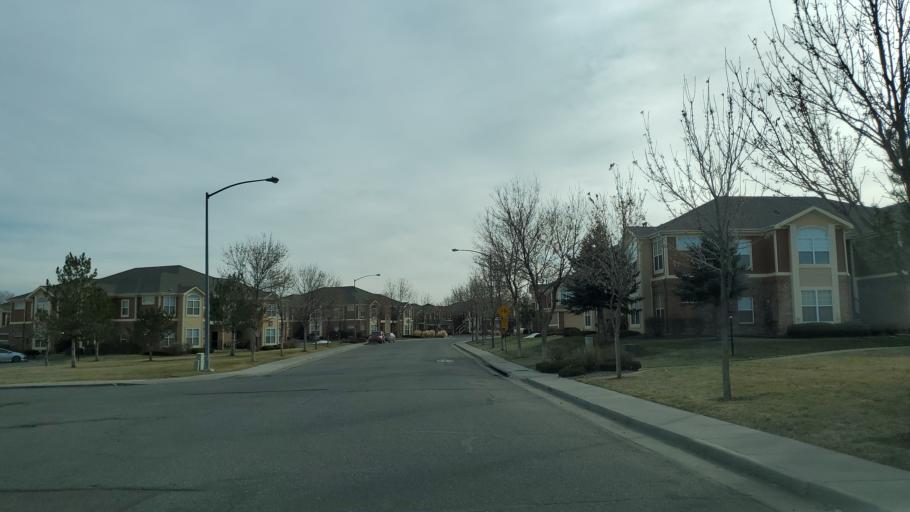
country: US
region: Colorado
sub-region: Adams County
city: Northglenn
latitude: 39.9158
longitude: -104.9472
